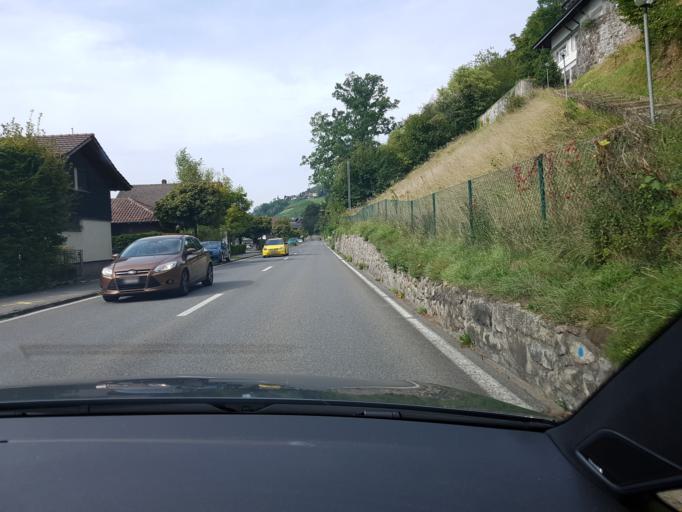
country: CH
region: Bern
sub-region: Thun District
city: Hilterfingen
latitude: 46.7221
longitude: 7.6843
